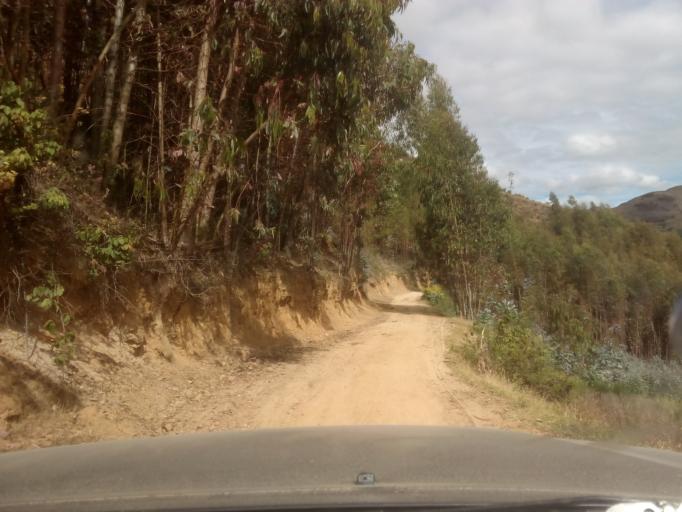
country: PE
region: La Libertad
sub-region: Sanchez Carrion
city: Curgos
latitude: -7.8705
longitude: -77.9536
